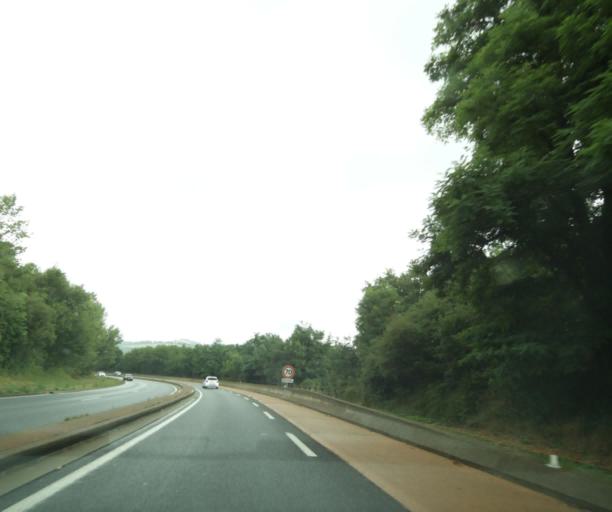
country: FR
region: Midi-Pyrenees
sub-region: Departement de l'Aveyron
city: Olemps
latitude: 44.3455
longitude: 2.5591
